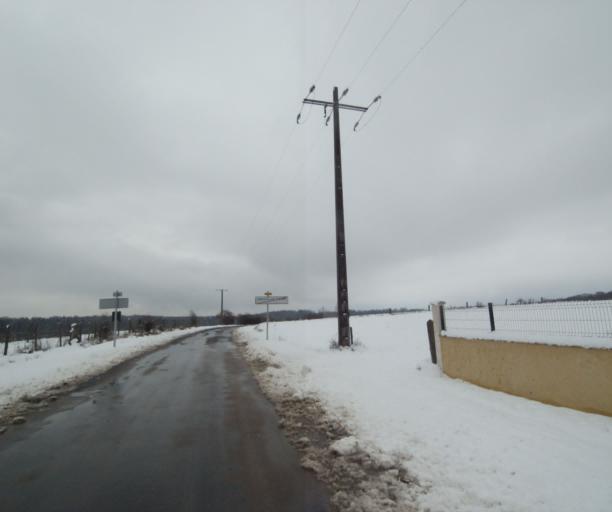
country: FR
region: Champagne-Ardenne
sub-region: Departement de la Haute-Marne
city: Laneuville-a-Remy
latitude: 48.4767
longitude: 4.8826
